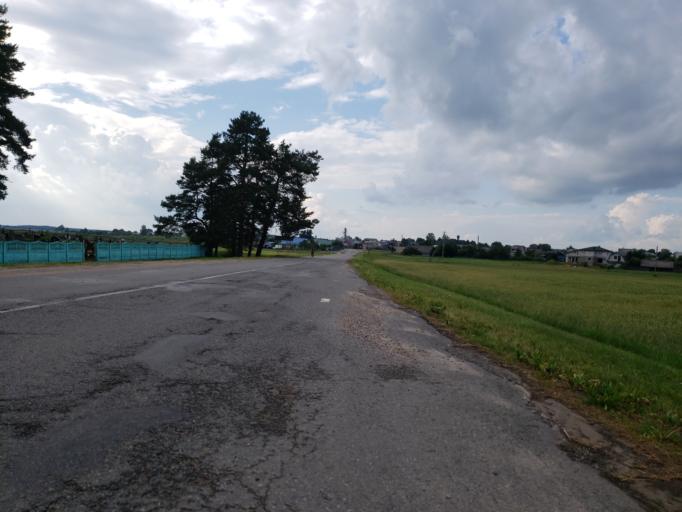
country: BY
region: Minsk
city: Chervyen'
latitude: 53.7272
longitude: 28.3908
